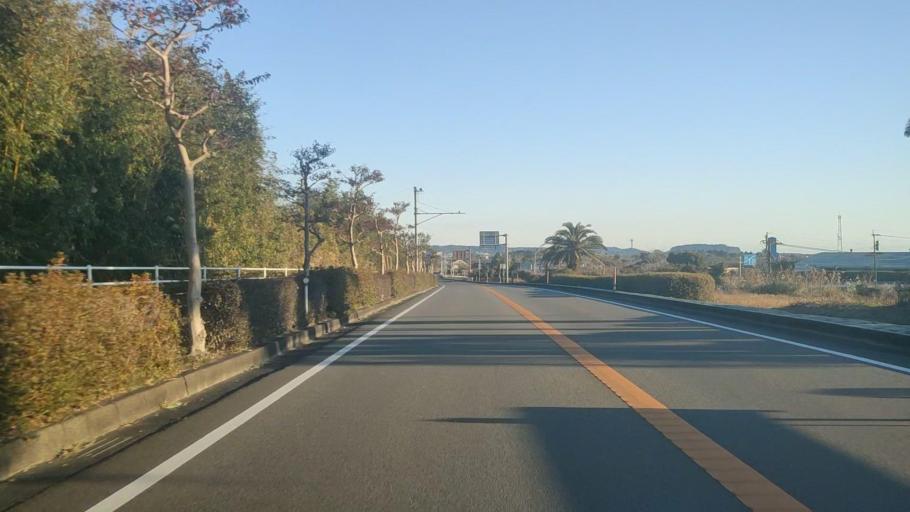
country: JP
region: Miyazaki
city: Tsuma
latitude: 32.0392
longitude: 131.4680
